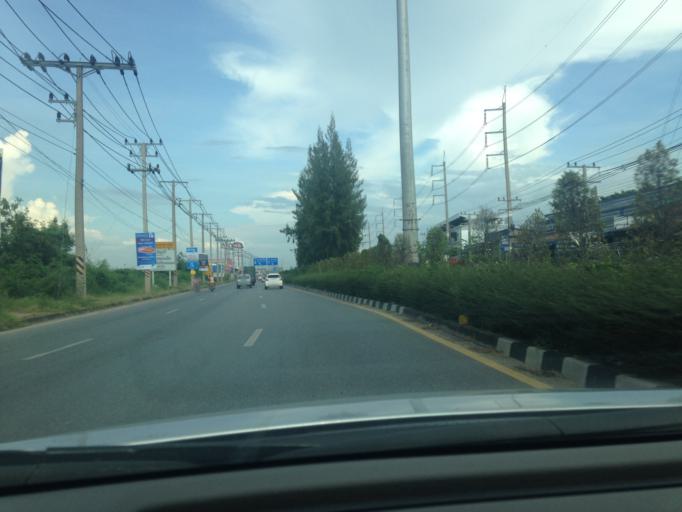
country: TH
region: Pathum Thani
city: Khlong Luang
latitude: 14.0668
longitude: 100.6885
